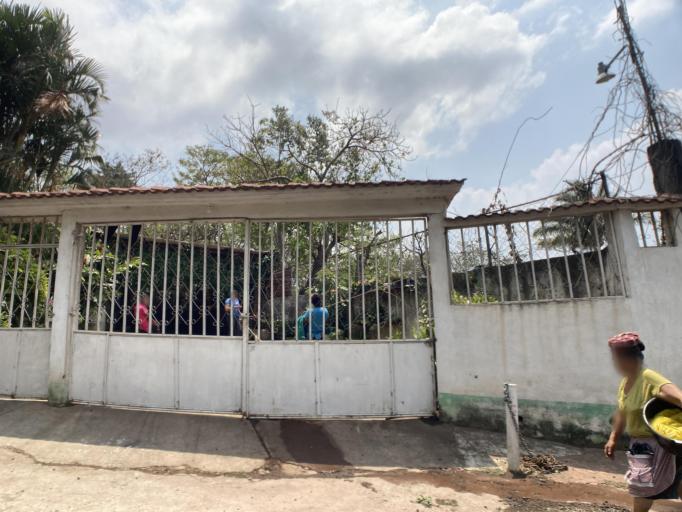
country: GT
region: Santa Rosa
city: Pueblo Nuevo Vinas
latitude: 14.3345
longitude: -90.5172
